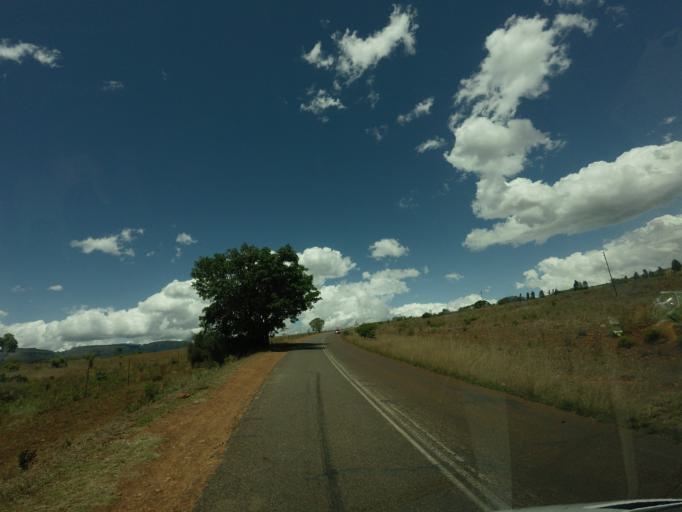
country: ZA
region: Limpopo
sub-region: Mopani District Municipality
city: Hoedspruit
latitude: -24.6082
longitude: 30.7908
